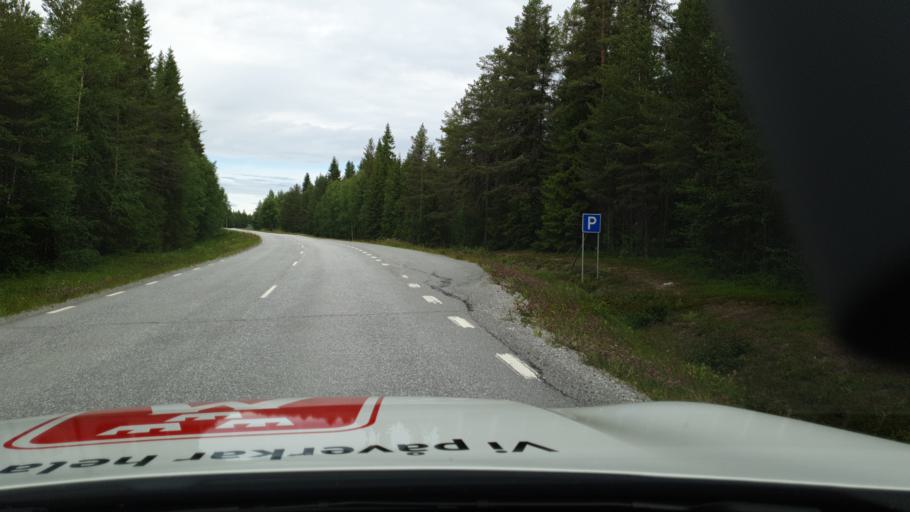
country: SE
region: Vaesterbotten
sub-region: Storumans Kommun
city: Storuman
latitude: 65.1984
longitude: 17.0058
